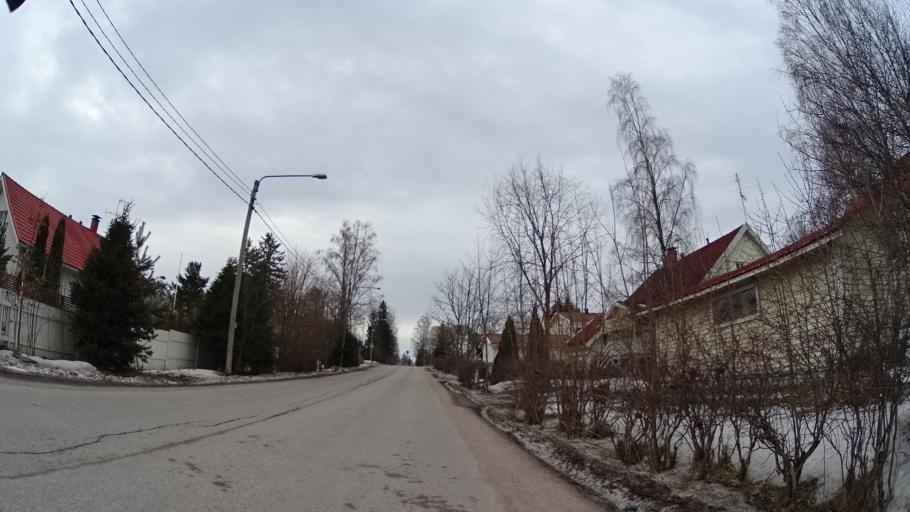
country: FI
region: Uusimaa
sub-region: Helsinki
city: Kilo
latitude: 60.2373
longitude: 24.8135
